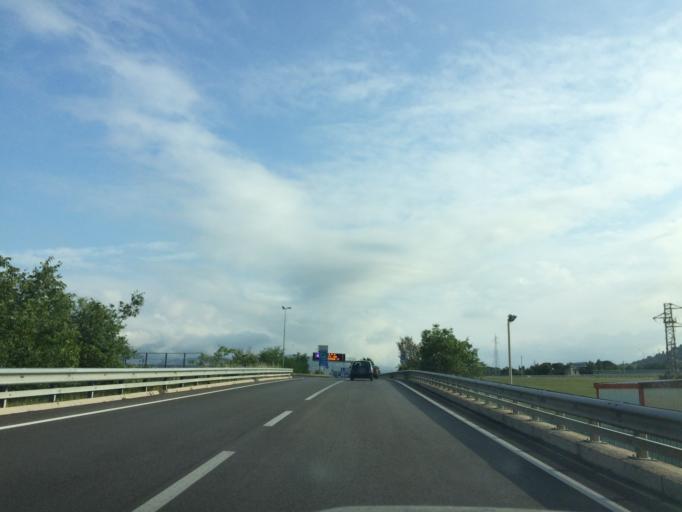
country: IT
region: Umbria
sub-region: Provincia di Perugia
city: Foligno
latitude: 42.9489
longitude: 12.7226
